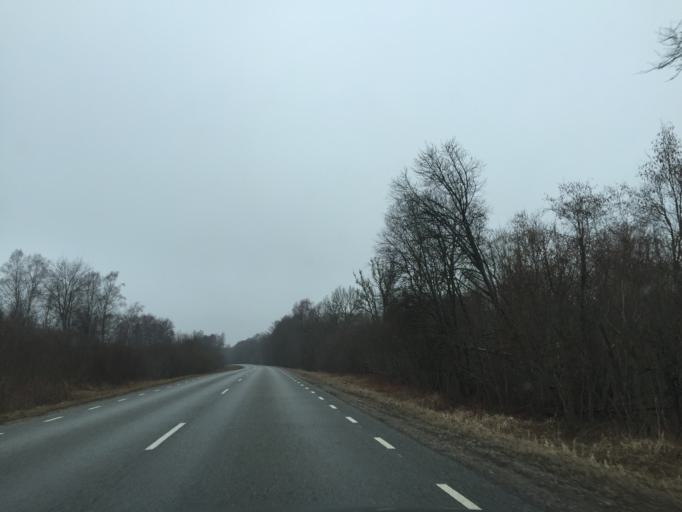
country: EE
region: Laeaene
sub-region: Lihula vald
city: Lihula
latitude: 58.5866
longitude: 23.7187
